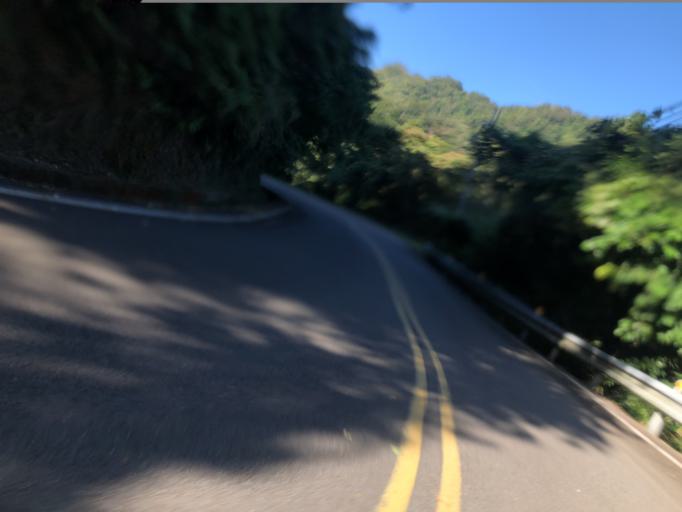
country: TW
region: Taiwan
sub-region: Miaoli
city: Miaoli
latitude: 24.5819
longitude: 120.9303
